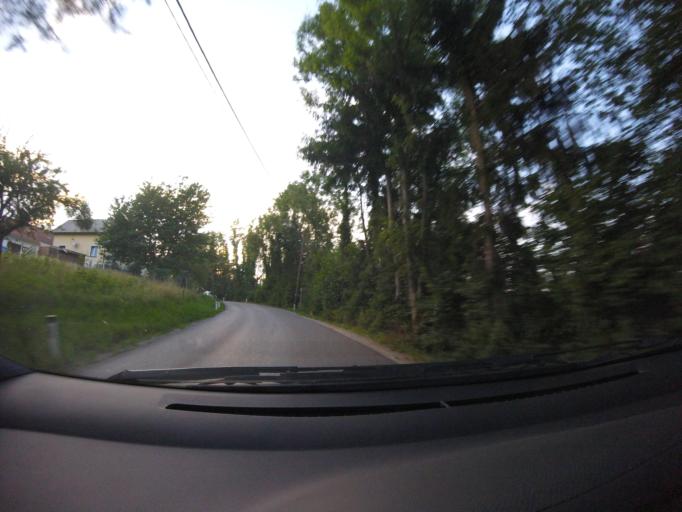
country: AT
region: Styria
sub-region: Politischer Bezirk Graz-Umgebung
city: Hart bei Graz
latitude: 47.0602
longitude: 15.5239
